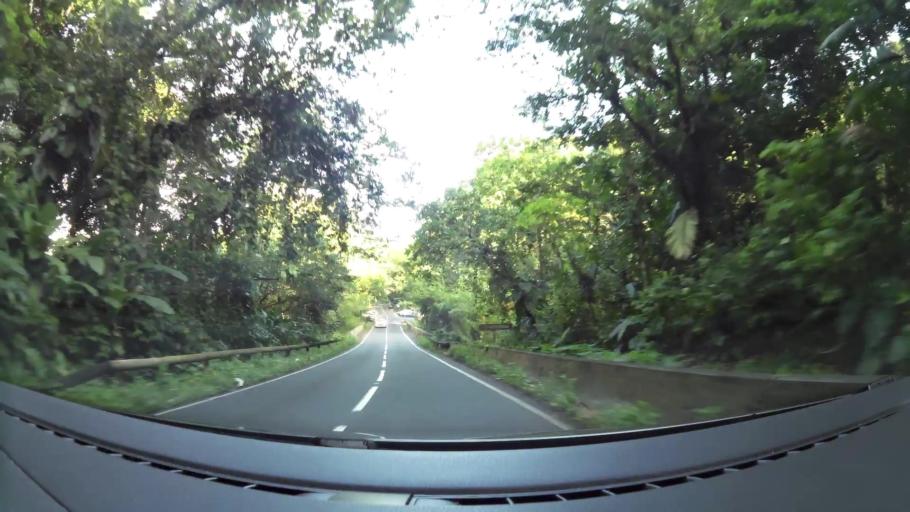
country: GP
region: Guadeloupe
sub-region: Guadeloupe
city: Petit-Bourg
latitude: 16.1796
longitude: -61.6810
